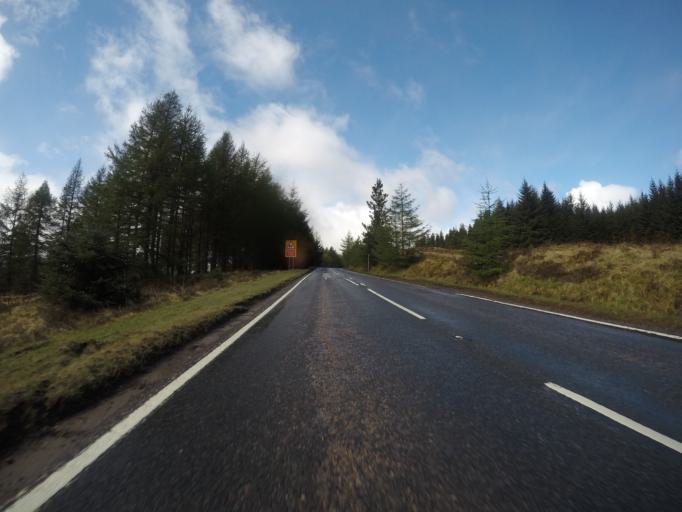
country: GB
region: Scotland
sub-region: Highland
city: Spean Bridge
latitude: 57.0876
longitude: -4.9753
